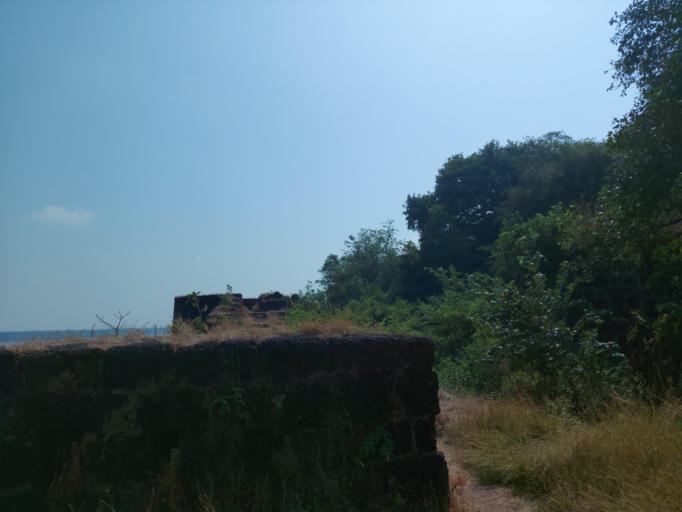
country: IN
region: Maharashtra
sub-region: Ratnagiri
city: Rajapur
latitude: 16.5618
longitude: 73.3338
